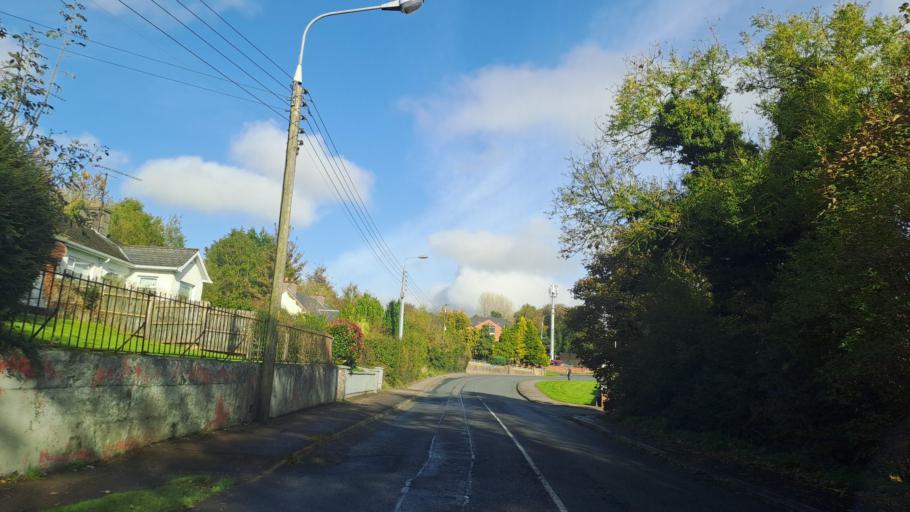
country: IE
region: Ulster
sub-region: An Cabhan
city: Cootehill
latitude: 54.0712
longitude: -7.0865
